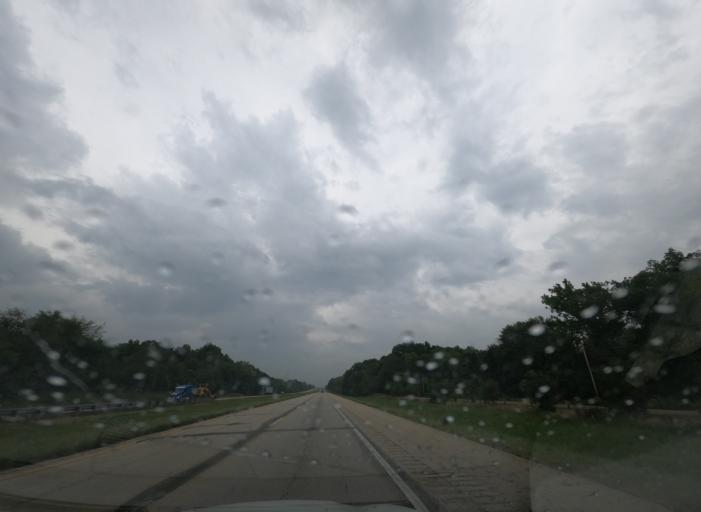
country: US
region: Illinois
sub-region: Effingham County
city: Teutopolis
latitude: 39.1526
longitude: -88.4853
